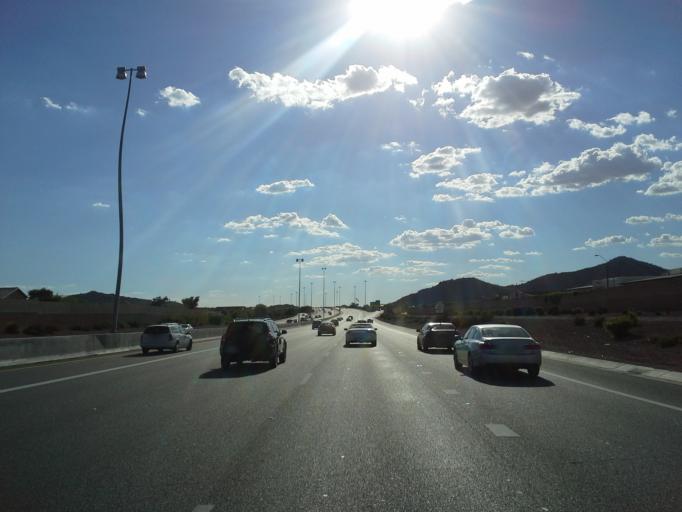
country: US
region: Arizona
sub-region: Maricopa County
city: Paradise Valley
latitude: 33.6729
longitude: -112.0210
